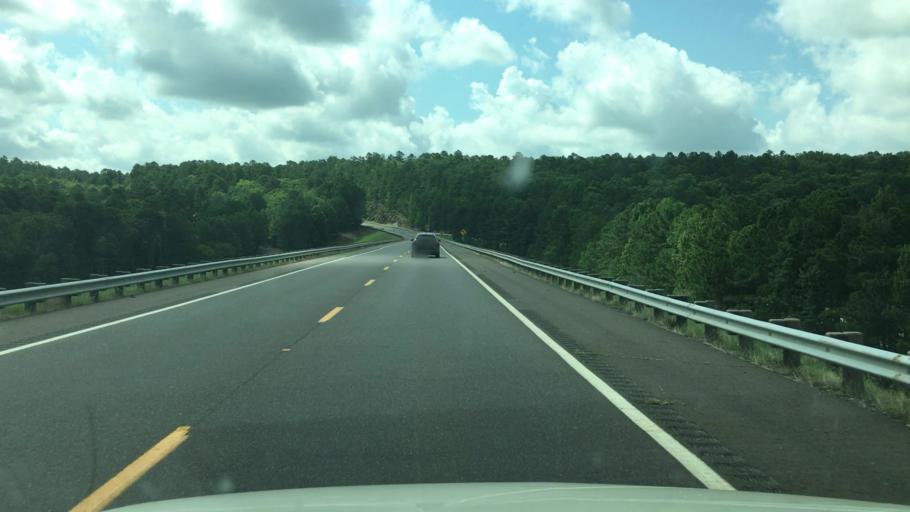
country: US
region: Arkansas
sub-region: Clark County
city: Arkadelphia
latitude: 34.2360
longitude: -93.1018
